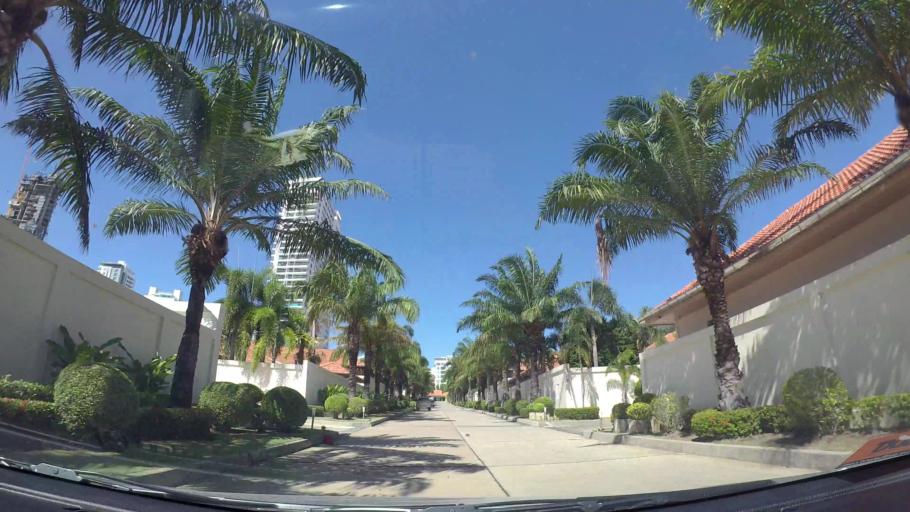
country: TH
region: Chon Buri
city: Phatthaya
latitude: 12.9166
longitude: 100.8587
